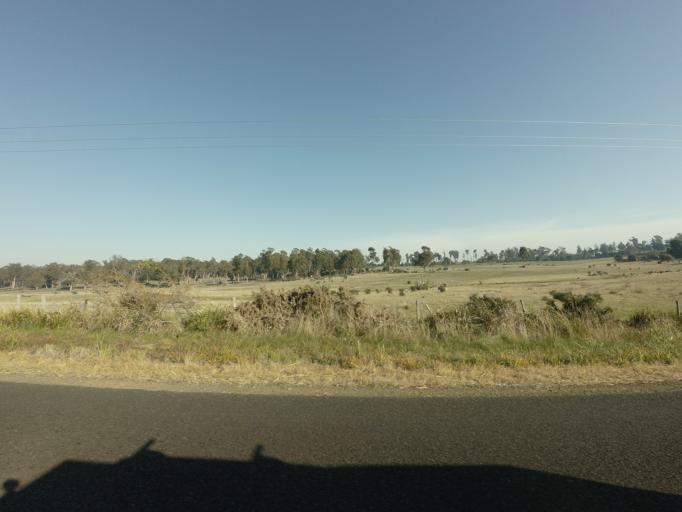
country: AU
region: Tasmania
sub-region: Northern Midlands
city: Longford
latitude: -41.5464
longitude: 146.9919
